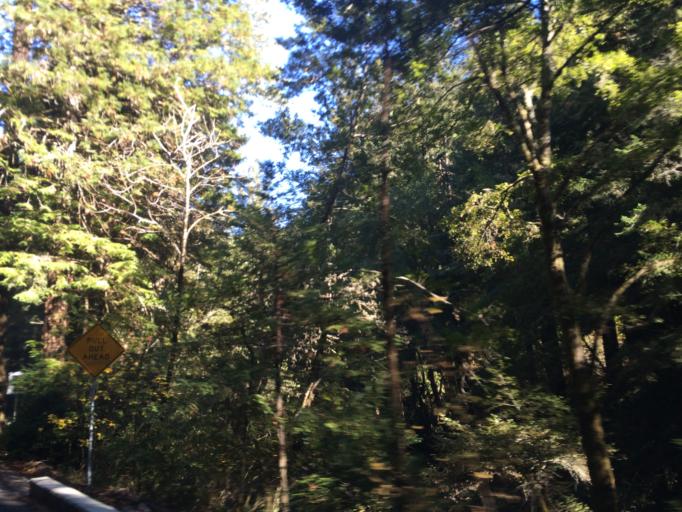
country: US
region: California
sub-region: Marin County
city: Lagunitas-Forest Knolls
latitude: 38.0056
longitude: -122.7115
